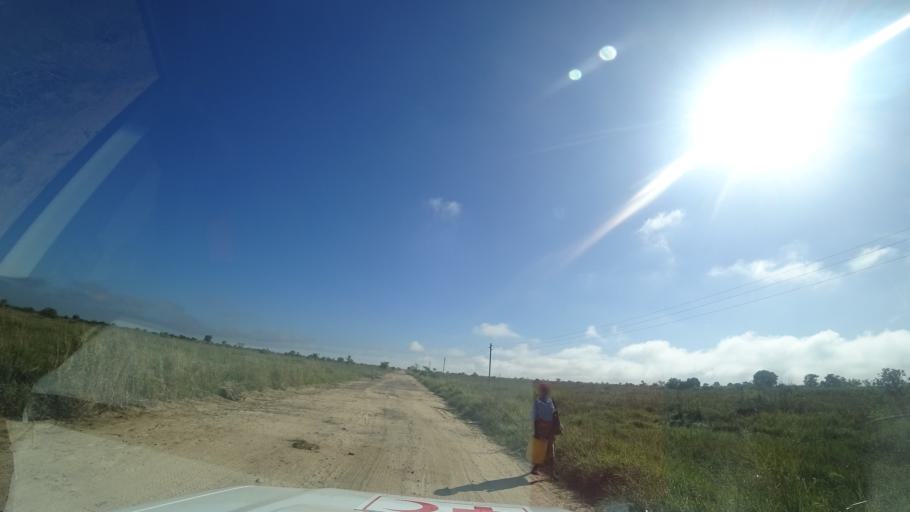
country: MZ
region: Sofala
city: Dondo
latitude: -19.4543
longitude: 34.5628
